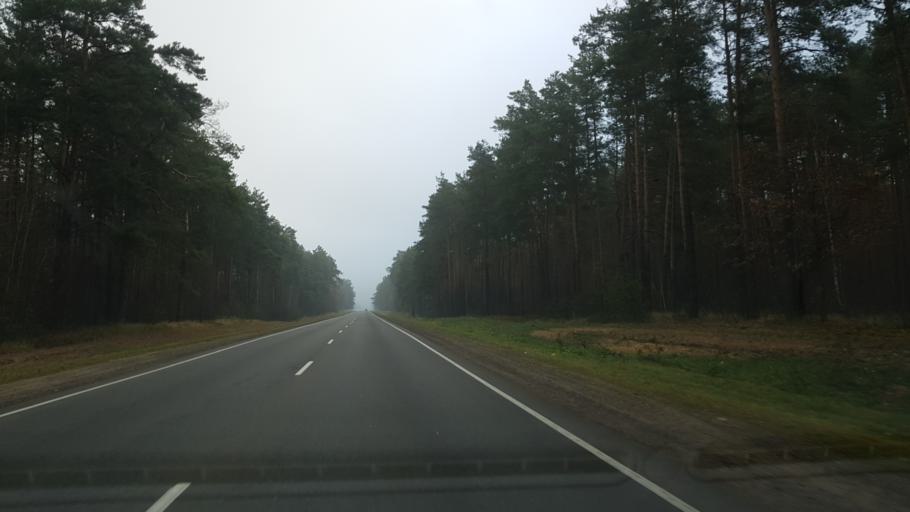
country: BY
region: Mogilev
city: Babruysk
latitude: 53.1631
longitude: 29.3261
